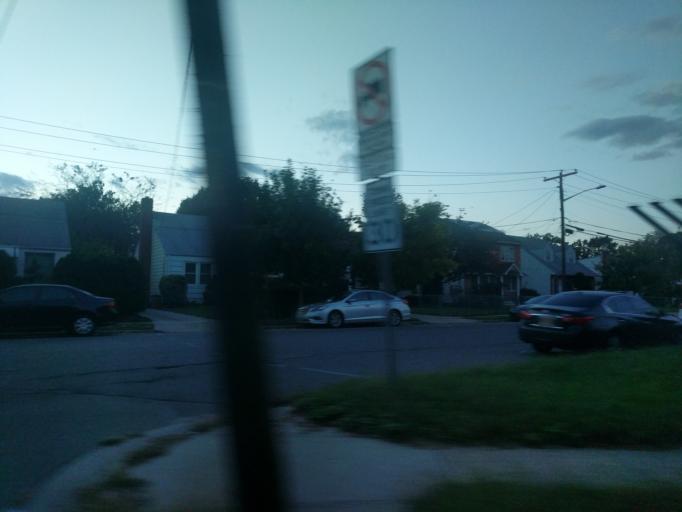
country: US
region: New York
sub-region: Nassau County
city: Garden City South
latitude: 40.6996
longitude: -73.6649
